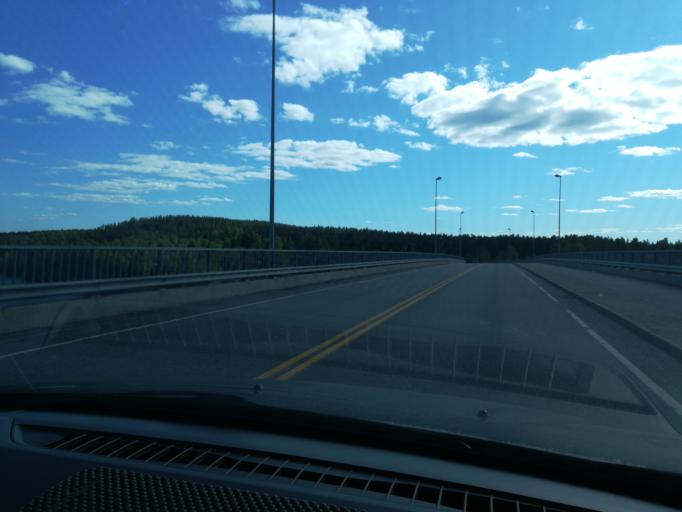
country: FI
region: Southern Savonia
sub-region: Mikkeli
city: Puumala
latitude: 61.5189
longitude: 28.1760
